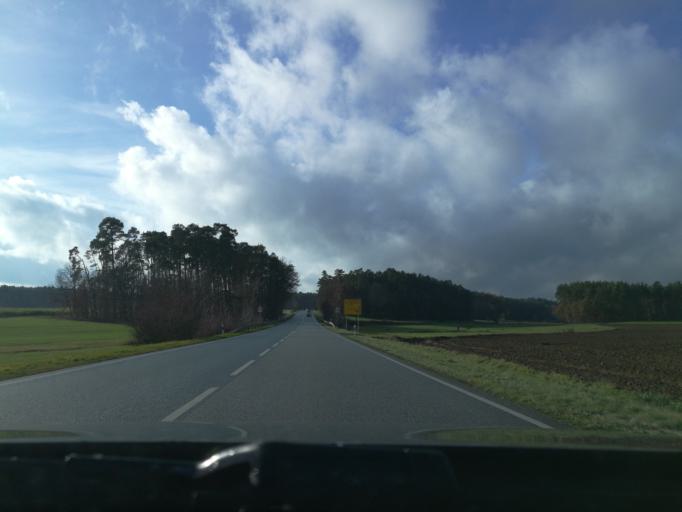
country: DE
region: Bavaria
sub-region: Regierungsbezirk Mittelfranken
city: Kammerstein
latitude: 49.2920
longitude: 10.9603
